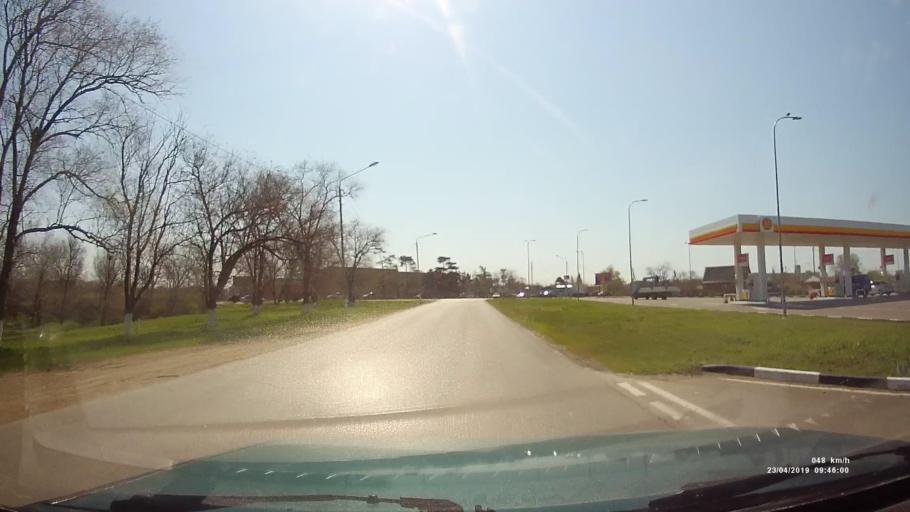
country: RU
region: Rostov
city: Orlovskiy
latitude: 46.8842
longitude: 42.0376
